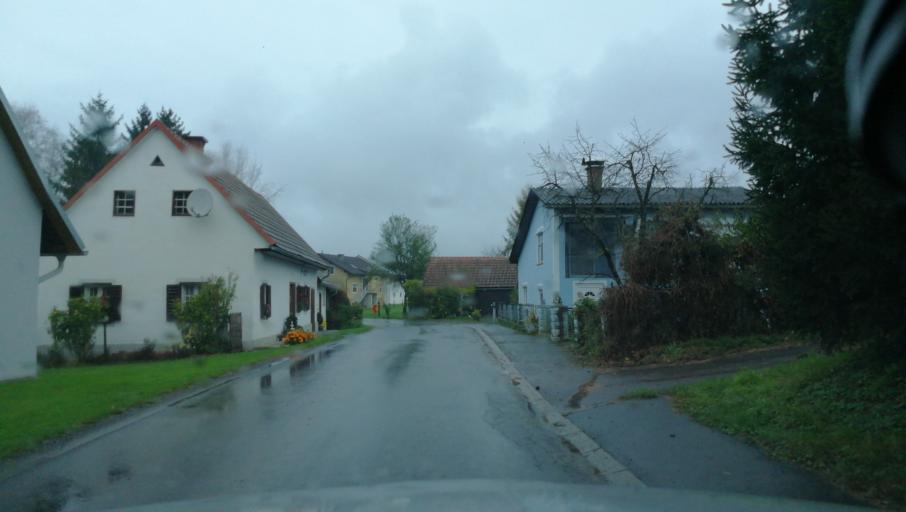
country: AT
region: Styria
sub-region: Politischer Bezirk Leibnitz
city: Strass in Steiermark
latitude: 46.7348
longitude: 15.6605
